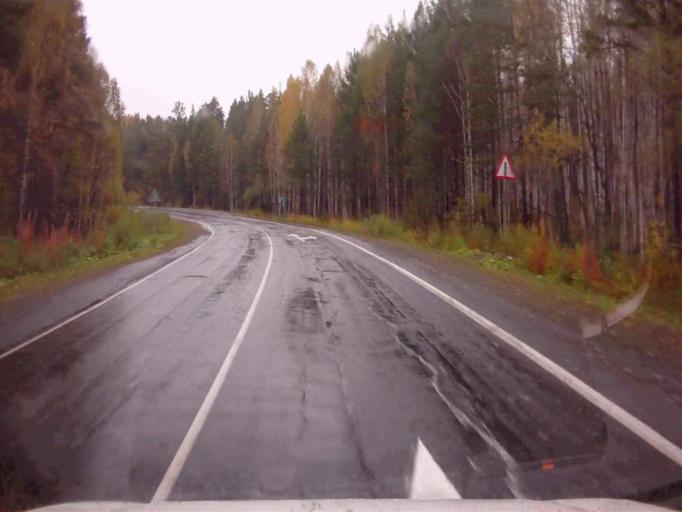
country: RU
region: Chelyabinsk
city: Verkhniy Ufaley
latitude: 55.9643
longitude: 60.3824
